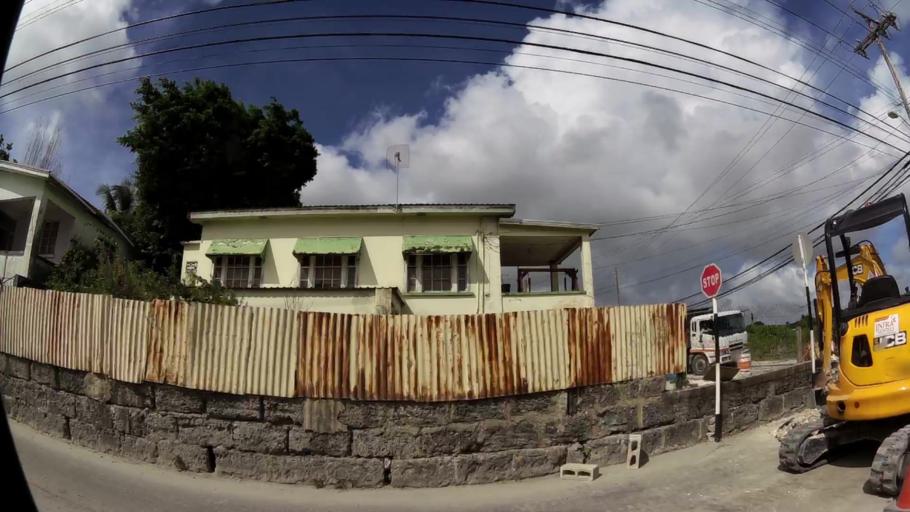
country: BB
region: Saint Michael
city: Bridgetown
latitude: 13.1005
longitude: -59.5925
